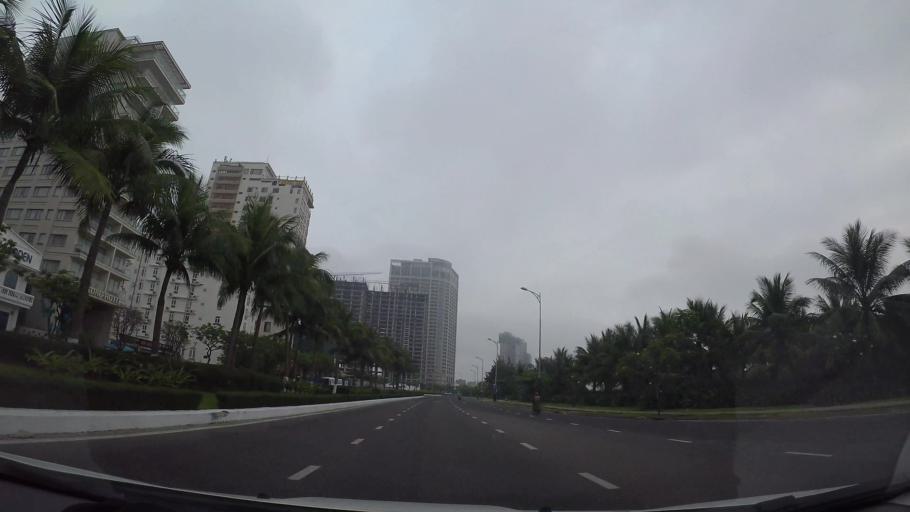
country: VN
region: Da Nang
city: Son Tra
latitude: 16.0745
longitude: 108.2452
